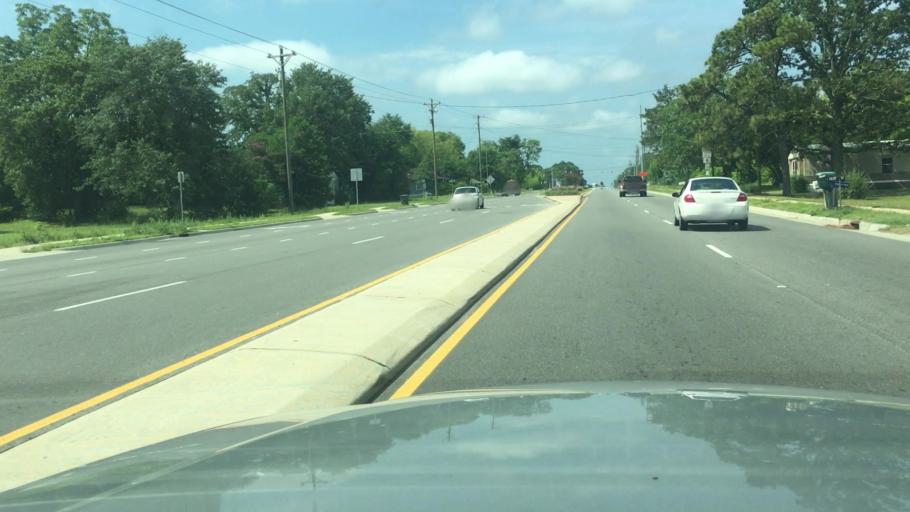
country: US
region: North Carolina
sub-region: Cumberland County
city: Fayetteville
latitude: 35.0174
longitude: -78.9049
